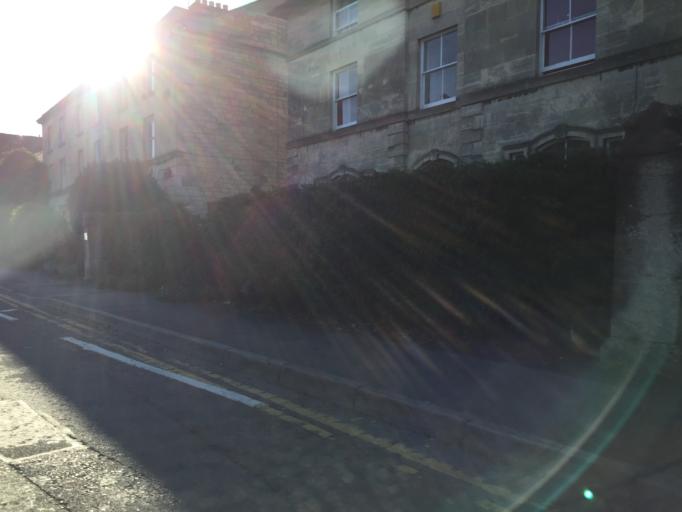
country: GB
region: England
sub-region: Gloucestershire
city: Stroud
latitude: 51.7437
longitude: -2.2403
